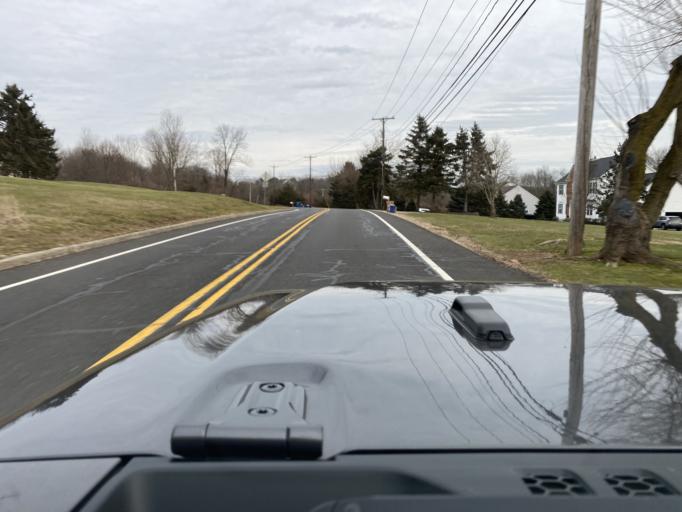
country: US
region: New Jersey
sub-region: Hunterdon County
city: Whitehouse Station
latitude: 40.5304
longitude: -74.7430
